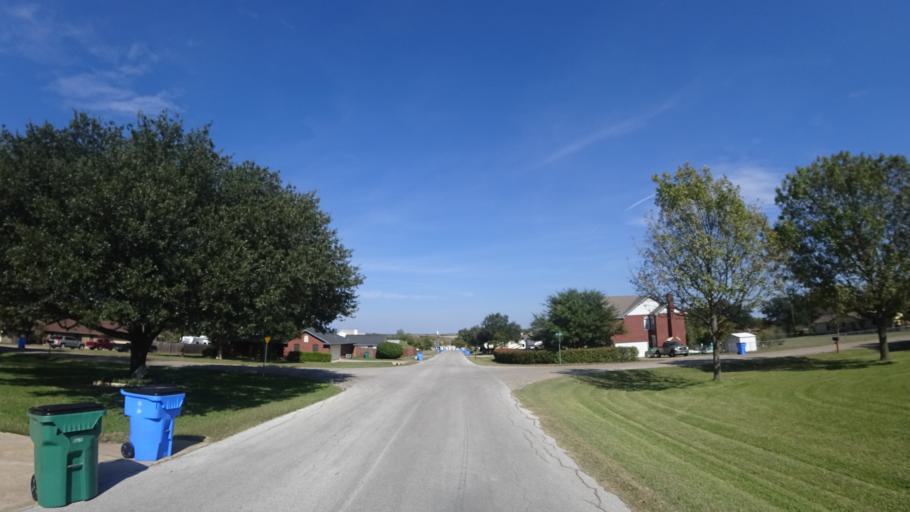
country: US
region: Texas
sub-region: Travis County
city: Pflugerville
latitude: 30.4199
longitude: -97.6264
